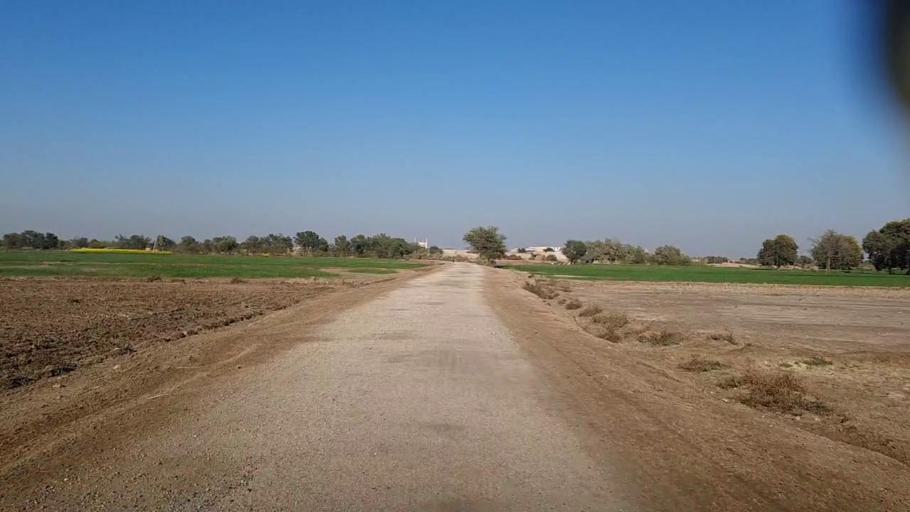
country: PK
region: Sindh
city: Khairpur
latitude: 27.8906
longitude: 69.7518
